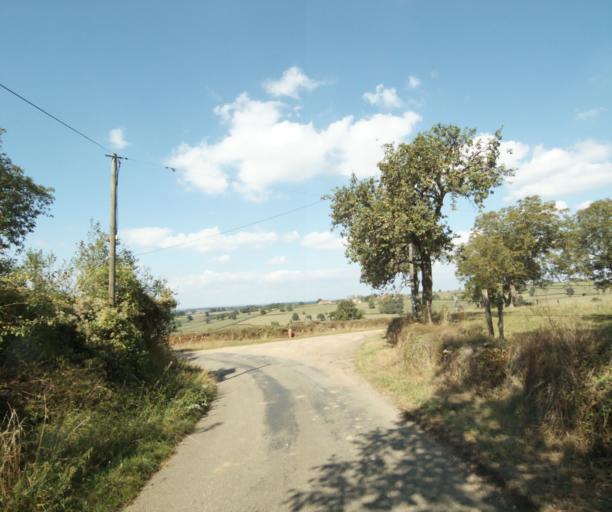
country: FR
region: Bourgogne
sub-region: Departement de Saone-et-Loire
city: Charolles
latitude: 46.3815
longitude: 4.2310
